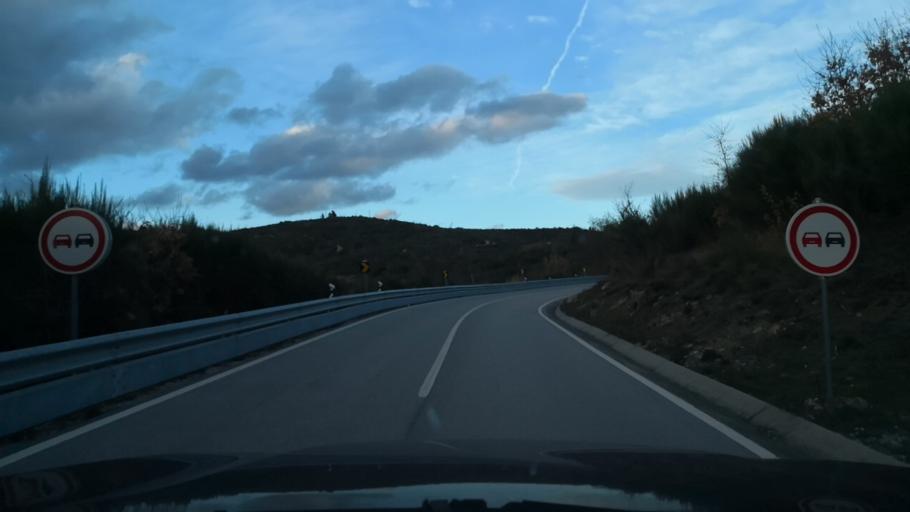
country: PT
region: Braganca
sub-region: Carrazeda de Ansiaes
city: Carrazeda de Anciaes
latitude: 41.2084
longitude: -7.3353
